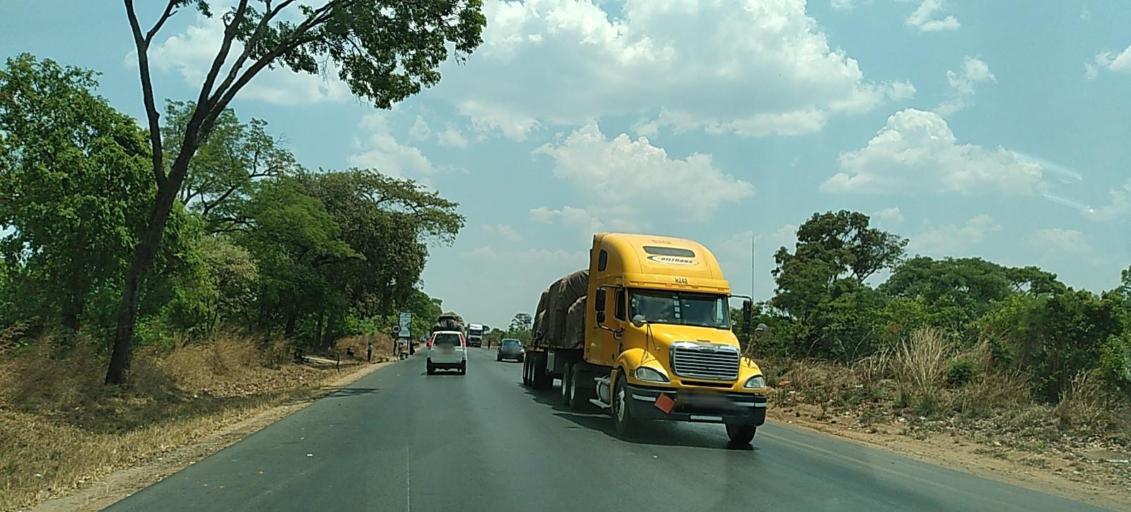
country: ZM
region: Central
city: Kabwe
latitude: -14.2458
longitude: 28.5645
